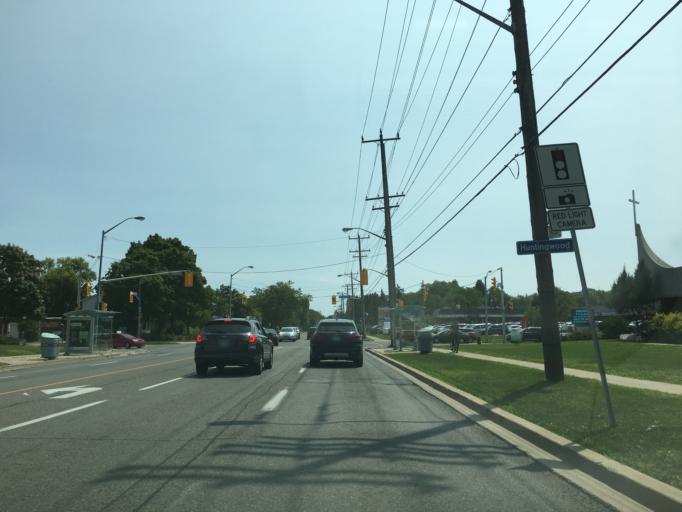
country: CA
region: Ontario
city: Scarborough
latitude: 43.7910
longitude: -79.3027
